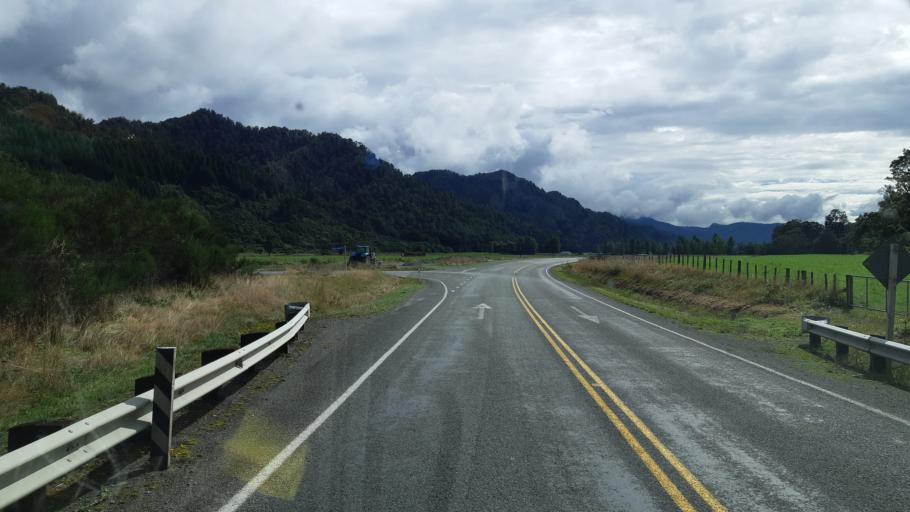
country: NZ
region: Tasman
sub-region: Tasman District
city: Wakefield
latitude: -41.7729
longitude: 172.3785
